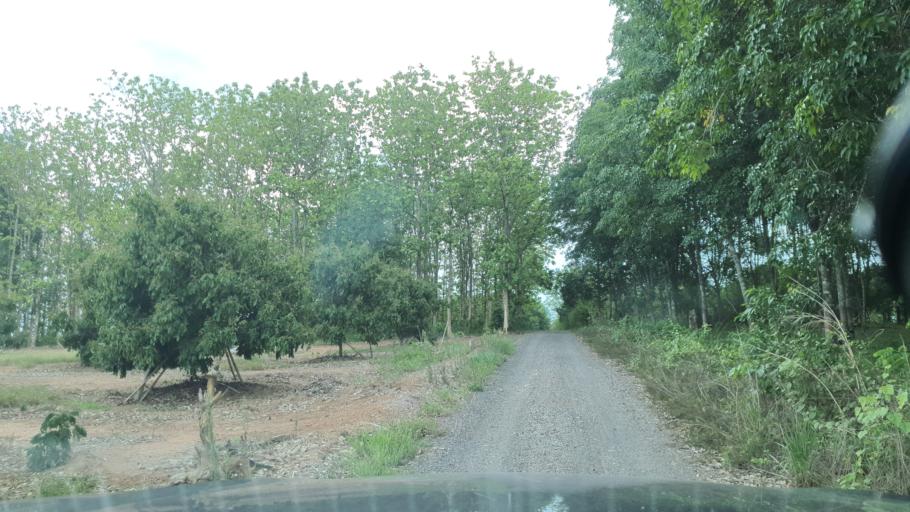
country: TH
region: Chiang Mai
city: Mae Taeng
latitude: 19.1262
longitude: 99.0466
